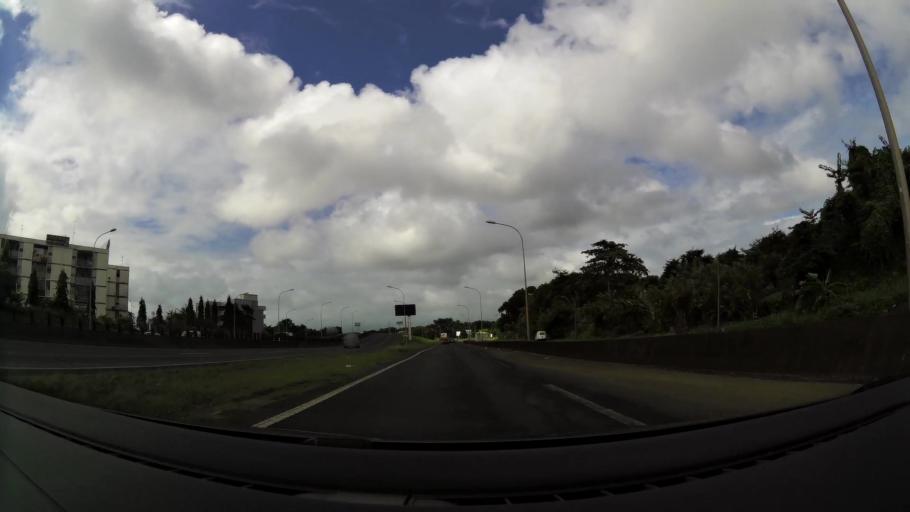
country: GP
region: Guadeloupe
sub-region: Guadeloupe
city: Pointe-a-Pitre
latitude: 16.2540
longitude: -61.5391
